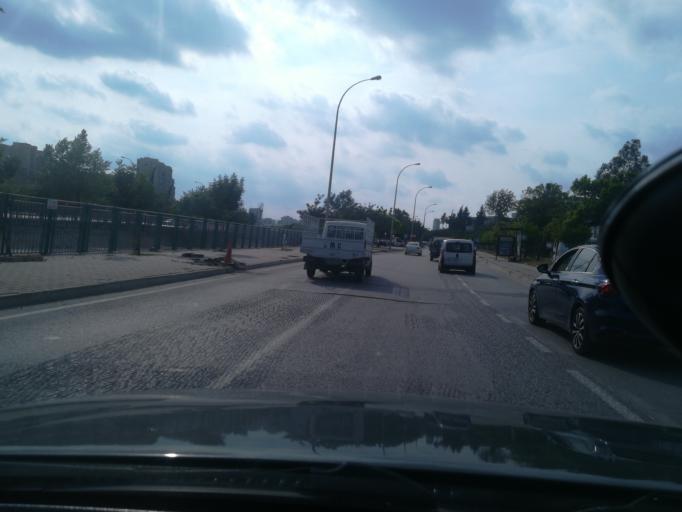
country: TR
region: Adana
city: Seyhan
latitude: 37.0116
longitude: 35.2842
